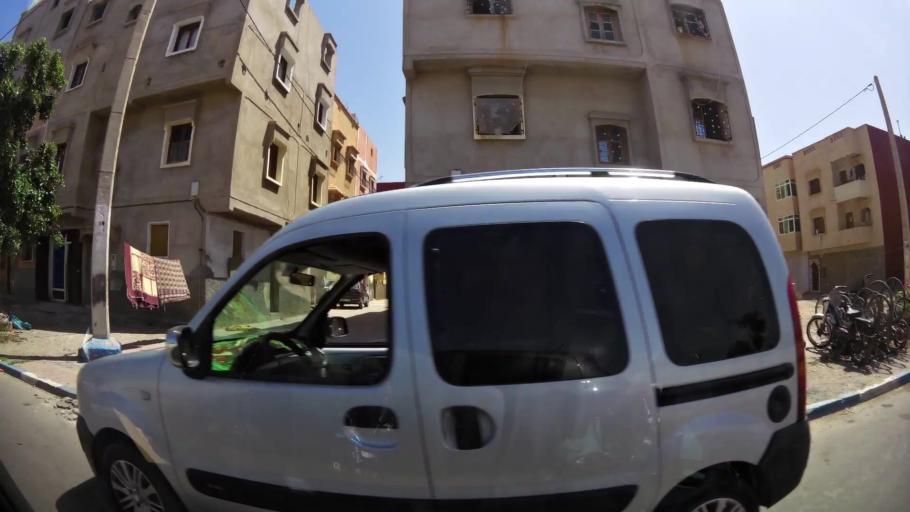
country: MA
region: Souss-Massa-Draa
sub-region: Inezgane-Ait Mellou
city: Inezgane
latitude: 30.3274
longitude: -9.5002
